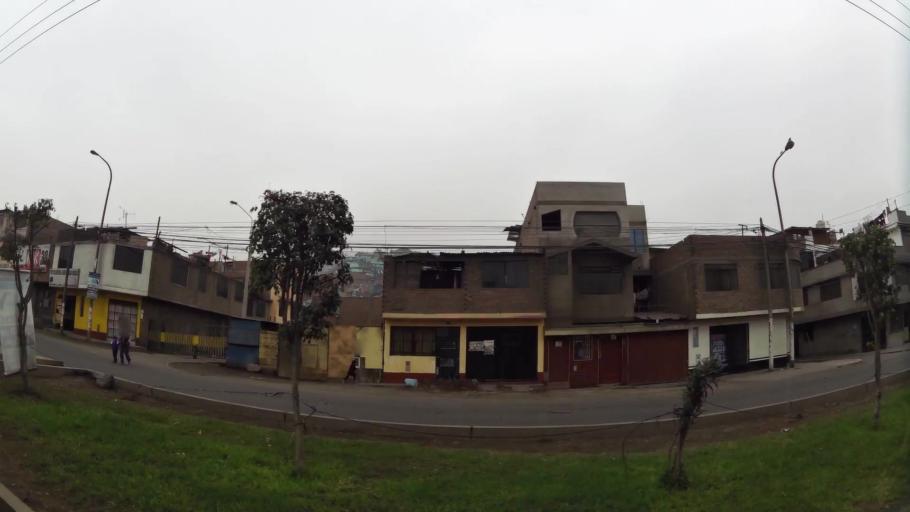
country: PE
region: Lima
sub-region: Lima
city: Independencia
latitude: -11.9447
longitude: -76.9768
